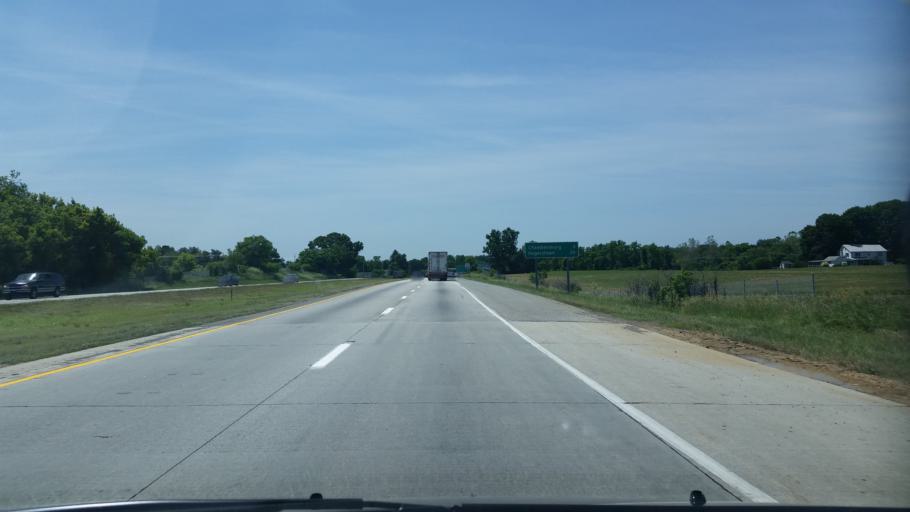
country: US
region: Pennsylvania
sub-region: Franklin County
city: Scotland
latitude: 39.9579
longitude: -77.5807
